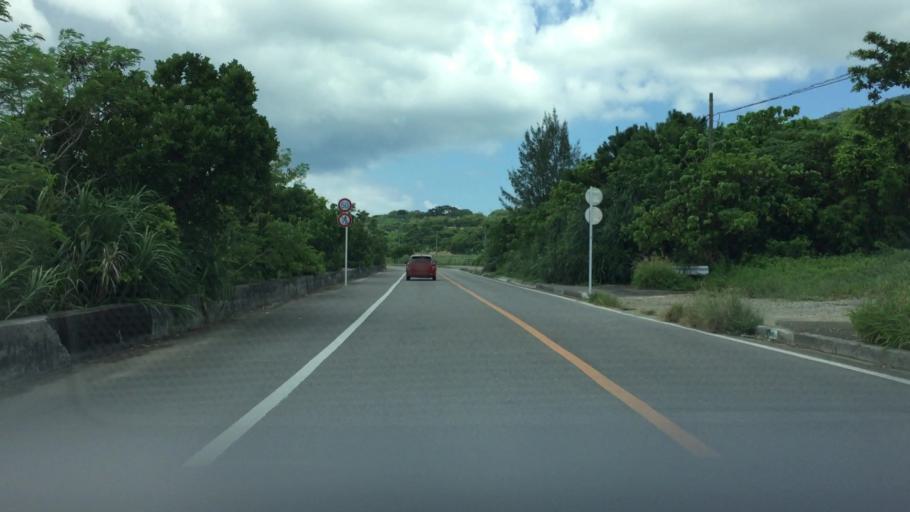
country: JP
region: Okinawa
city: Ishigaki
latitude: 24.4208
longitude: 124.1334
